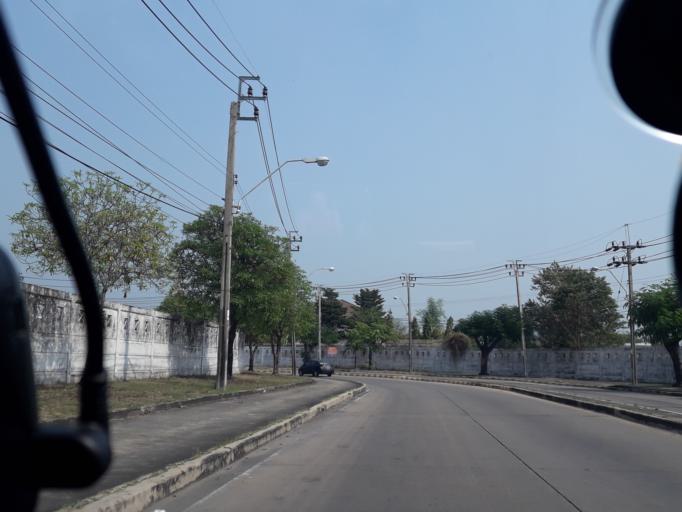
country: TH
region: Bangkok
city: Khan Na Yao
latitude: 13.8444
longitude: 100.6986
